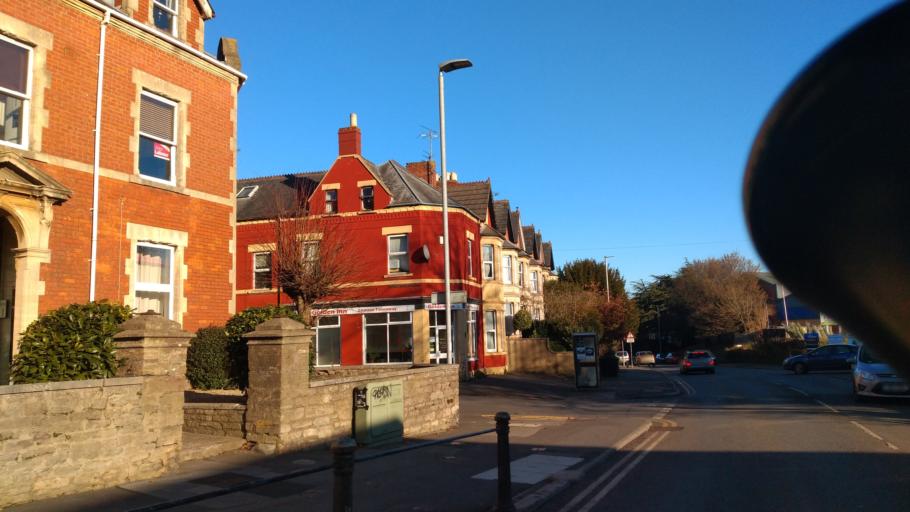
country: GB
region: England
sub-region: Somerset
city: Frome
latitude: 51.2276
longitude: -2.3119
